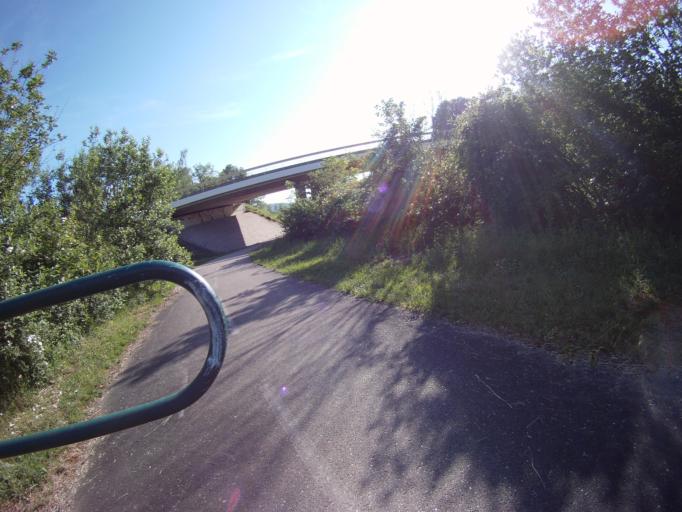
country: FR
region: Lorraine
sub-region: Departement de Meurthe-et-Moselle
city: Lay-Saint-Christophe
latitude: 48.7436
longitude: 6.1842
